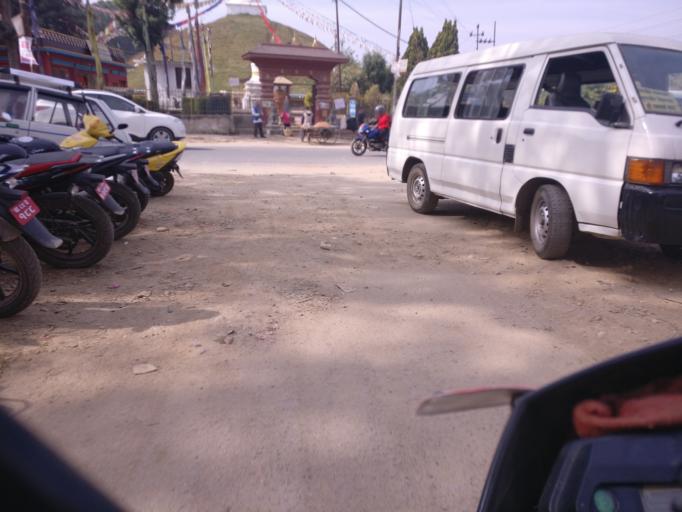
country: NP
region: Central Region
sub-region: Bagmati Zone
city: Patan
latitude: 27.6648
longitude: 85.3241
